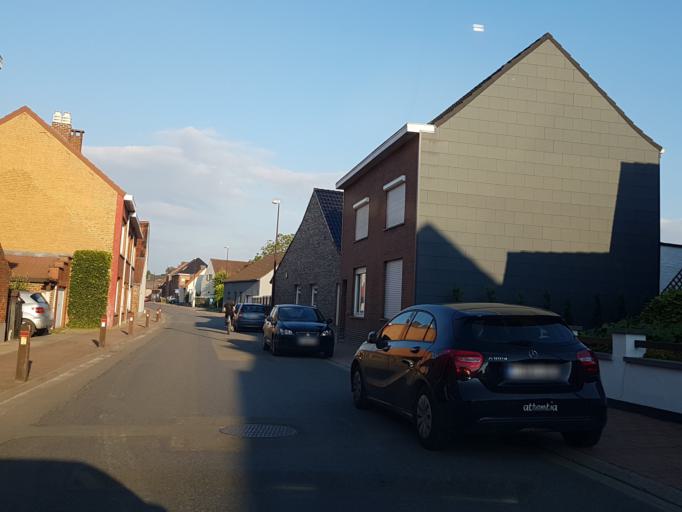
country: BE
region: Flanders
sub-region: Provincie Vlaams-Brabant
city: Ternat
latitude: 50.8820
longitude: 4.1332
